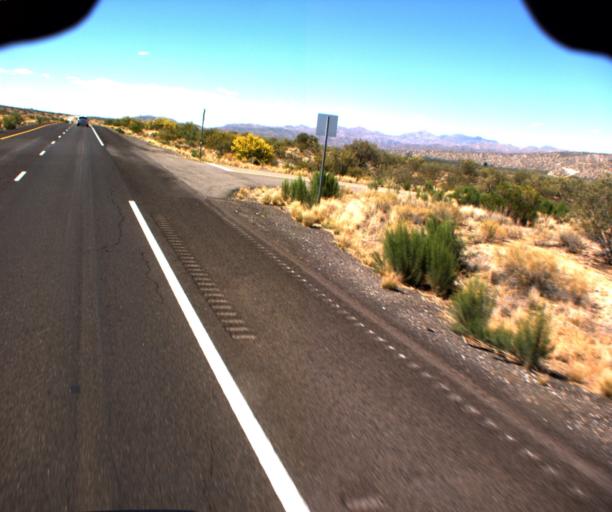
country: US
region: Arizona
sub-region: Yavapai County
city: Bagdad
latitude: 34.8478
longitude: -113.6367
